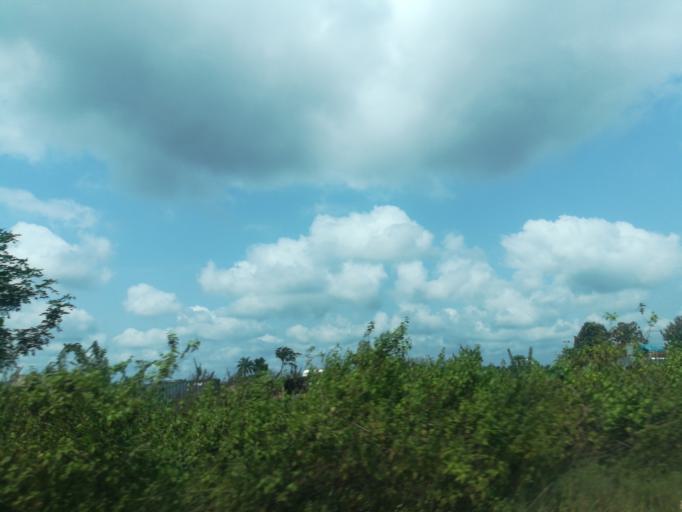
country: NG
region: Oyo
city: Moniya
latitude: 7.5811
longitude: 3.9153
